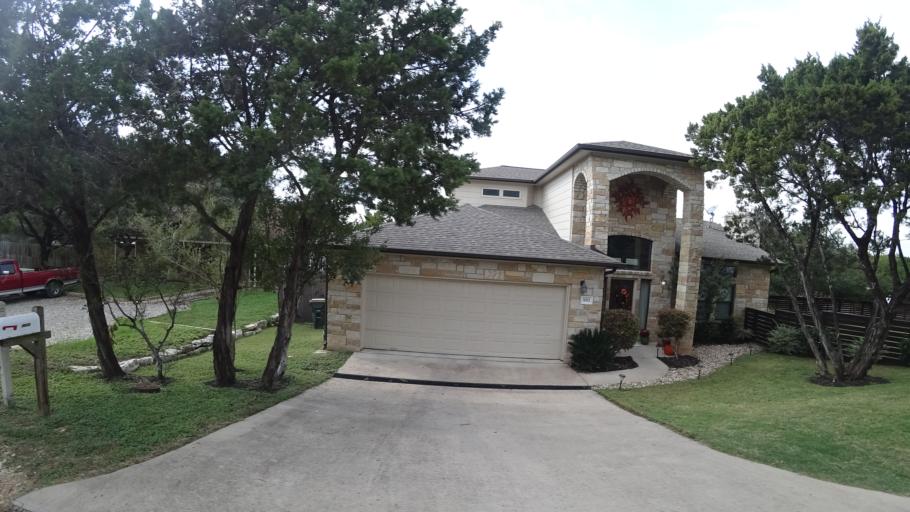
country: US
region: Texas
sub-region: Travis County
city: Hudson Bend
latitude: 30.3828
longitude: -97.9178
